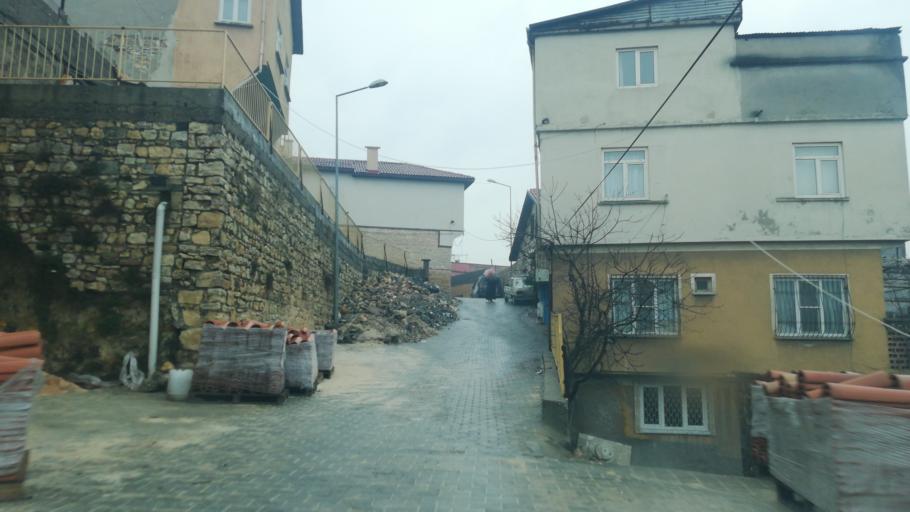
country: TR
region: Kahramanmaras
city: Kahramanmaras
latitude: 37.5866
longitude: 36.9325
